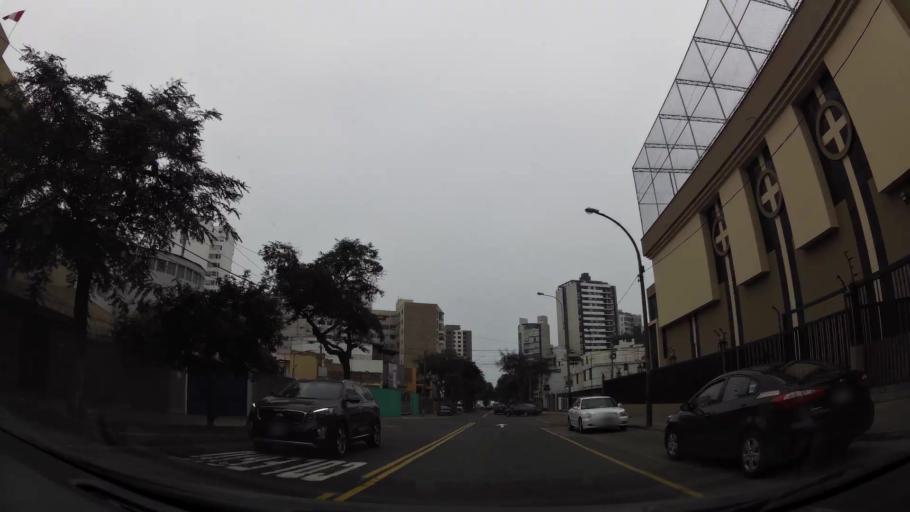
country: PE
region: Lima
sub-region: Lima
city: San Isidro
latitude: -12.1175
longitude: -77.0422
